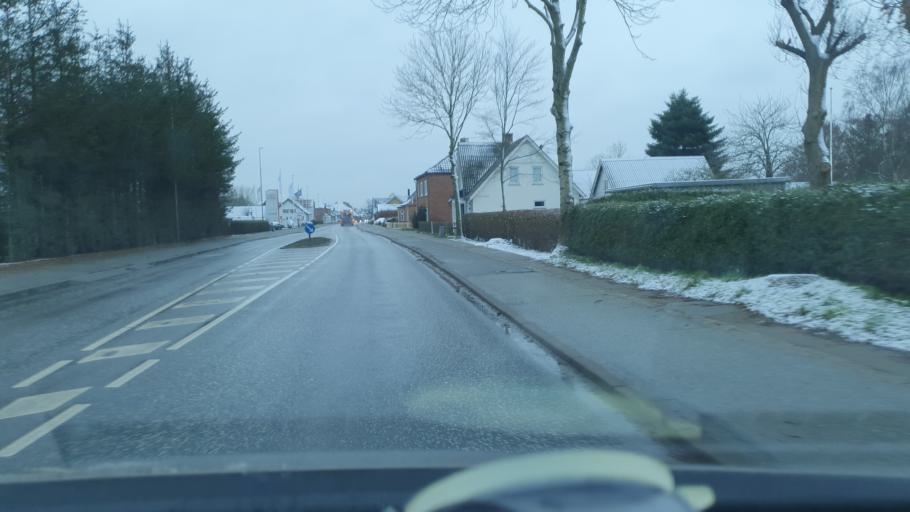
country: DK
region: North Denmark
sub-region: Jammerbugt Kommune
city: Brovst
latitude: 57.1114
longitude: 9.5924
